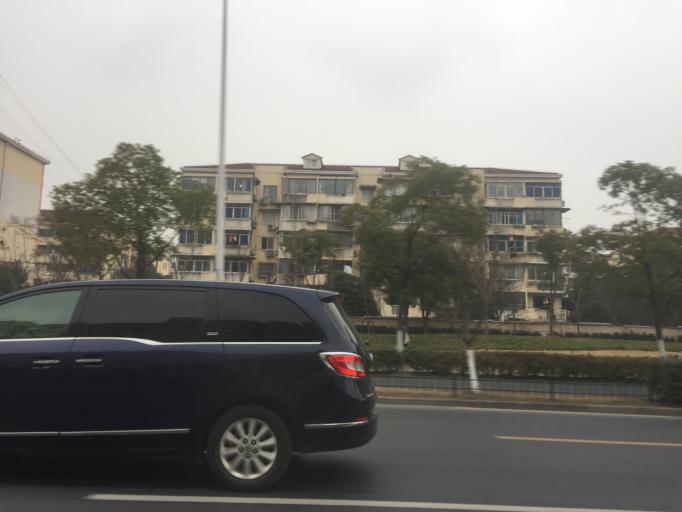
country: CN
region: Shanghai Shi
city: Huamu
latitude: 31.1898
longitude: 121.5149
